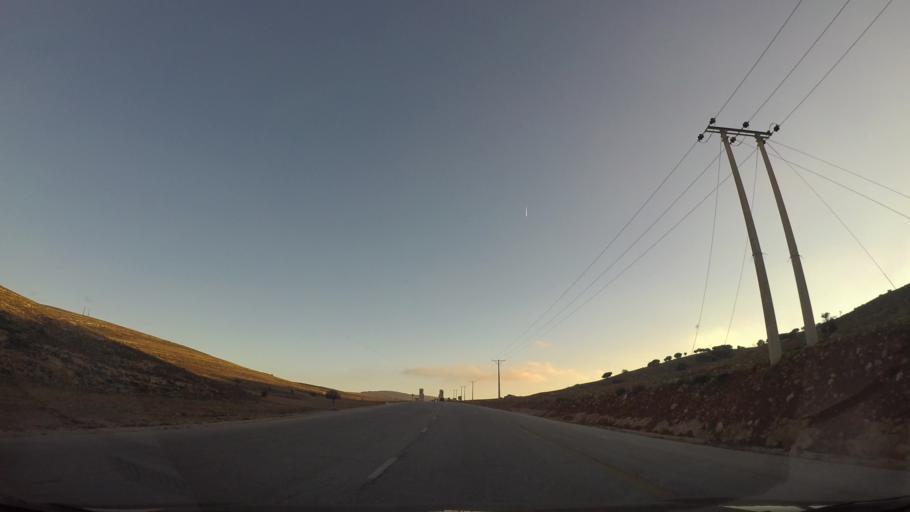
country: JO
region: Ma'an
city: Petra
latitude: 30.4065
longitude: 35.5042
